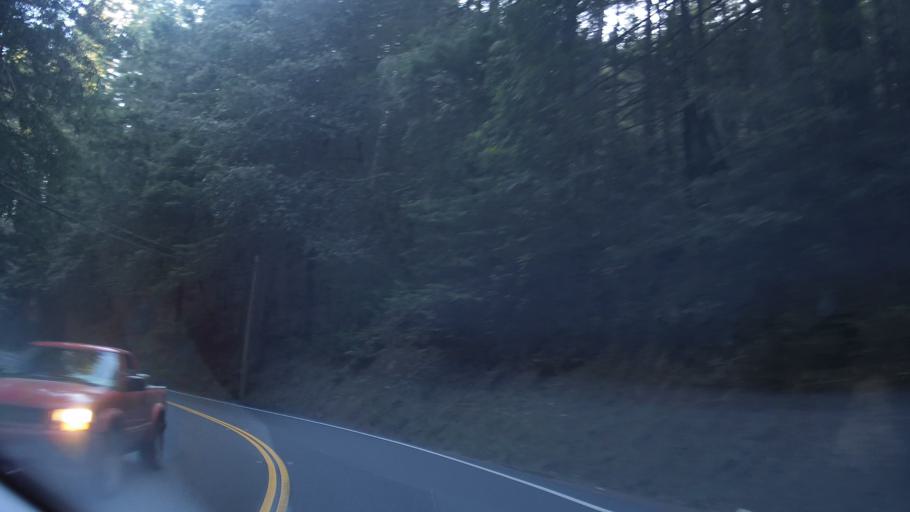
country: US
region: California
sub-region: Mendocino County
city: Fort Bragg
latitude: 39.4067
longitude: -123.7333
